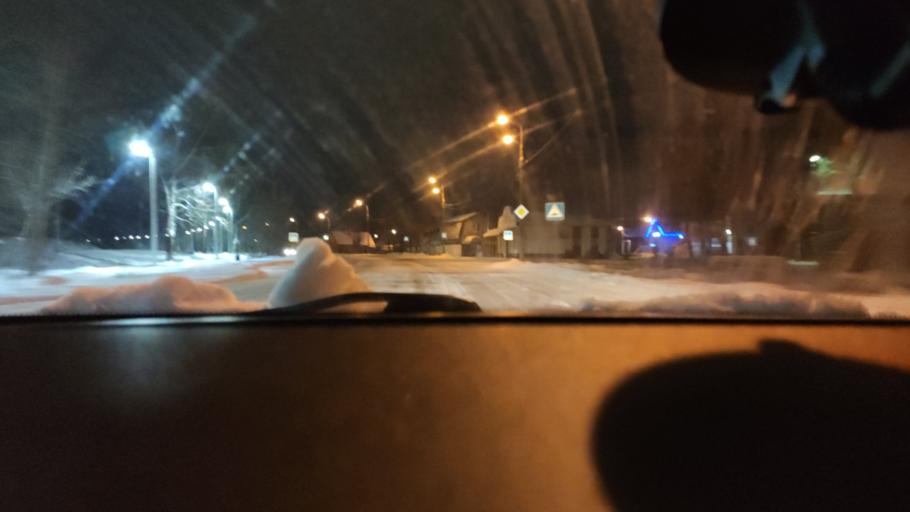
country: RU
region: Perm
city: Krasnokamsk
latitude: 58.0618
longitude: 55.8035
